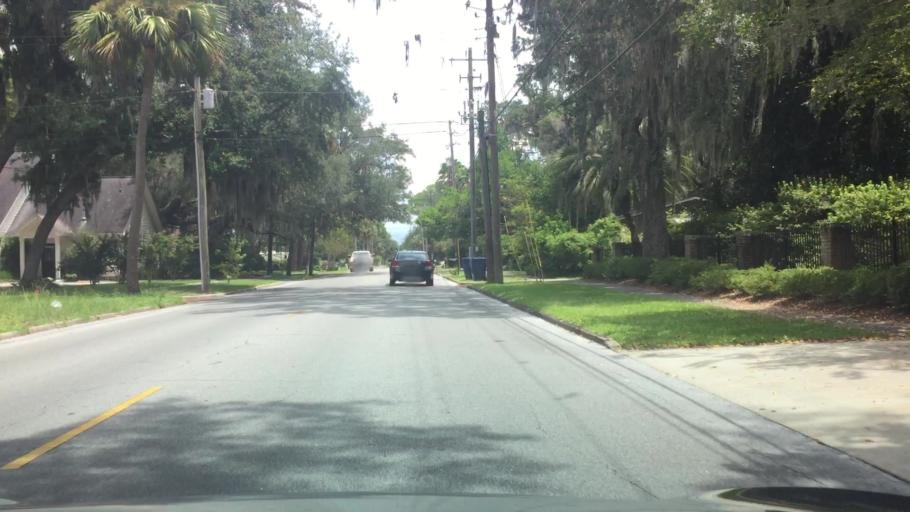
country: US
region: Florida
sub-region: Bay County
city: Panama City
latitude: 30.1459
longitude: -85.6532
